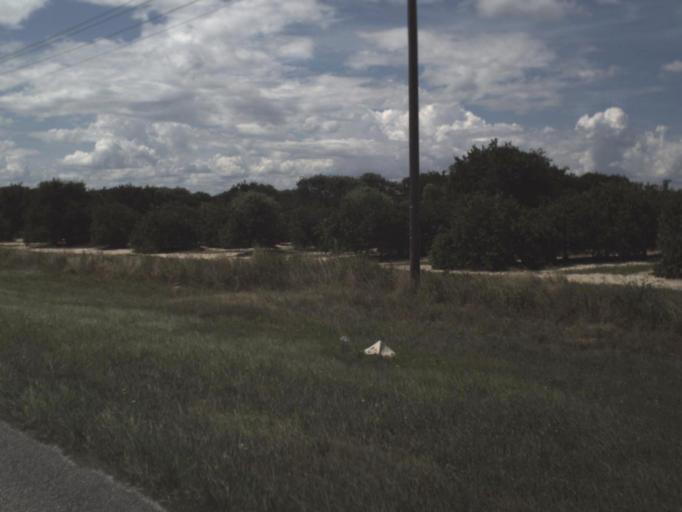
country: US
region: Florida
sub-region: Polk County
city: Babson Park
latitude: 27.8943
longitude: -81.4991
